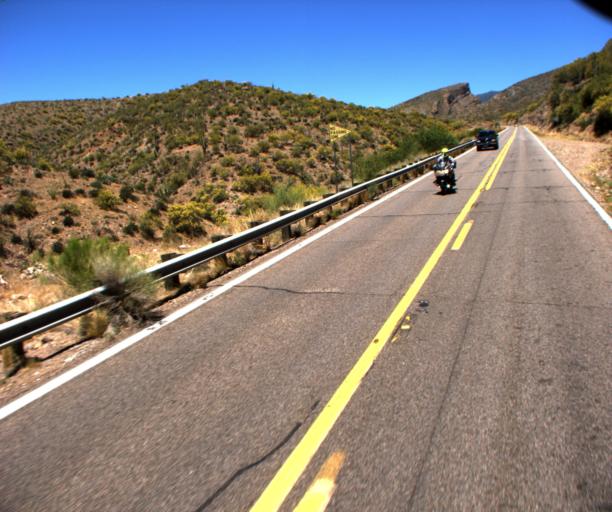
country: US
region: Arizona
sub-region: Pinal County
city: Kearny
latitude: 33.1641
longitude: -110.8051
